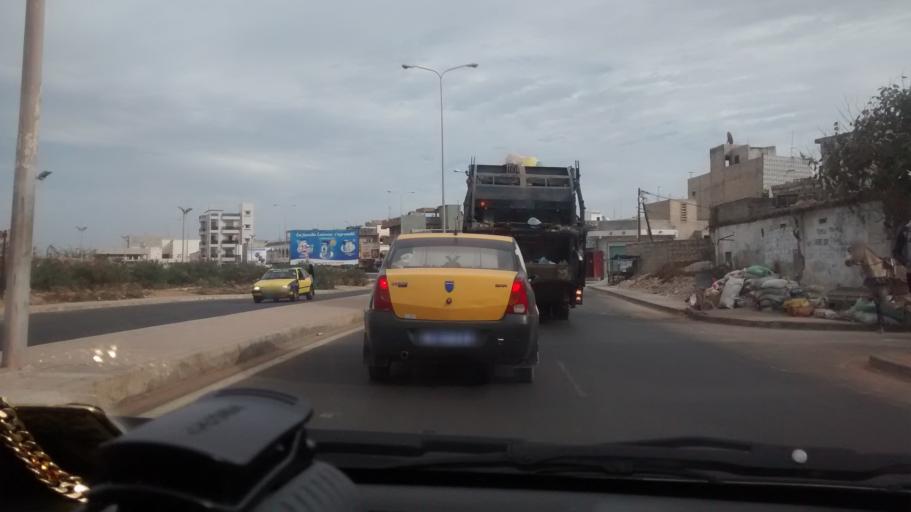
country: SN
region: Dakar
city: Pikine
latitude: 14.7717
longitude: -17.4081
